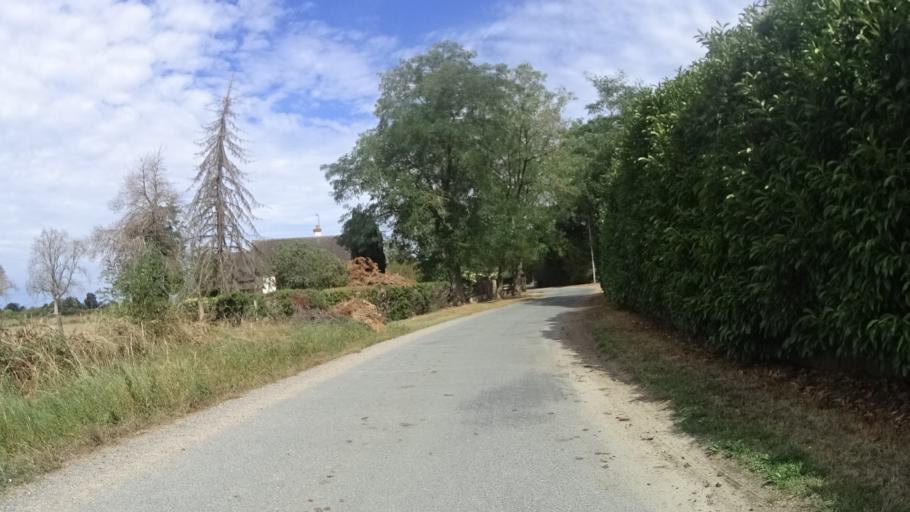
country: FR
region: Auvergne
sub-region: Departement de l'Allier
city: Beaulon
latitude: 46.6499
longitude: 3.6877
